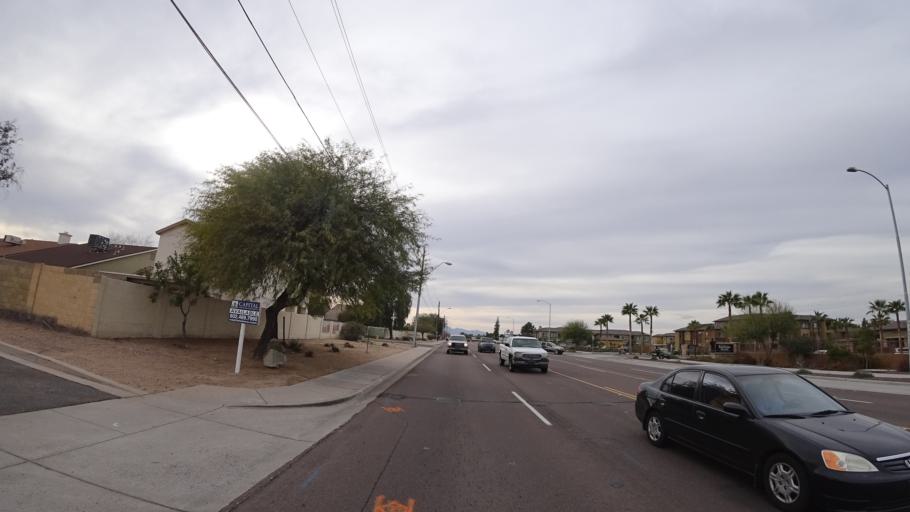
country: US
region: Arizona
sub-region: Maricopa County
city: Peoria
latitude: 33.5813
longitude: -112.2227
